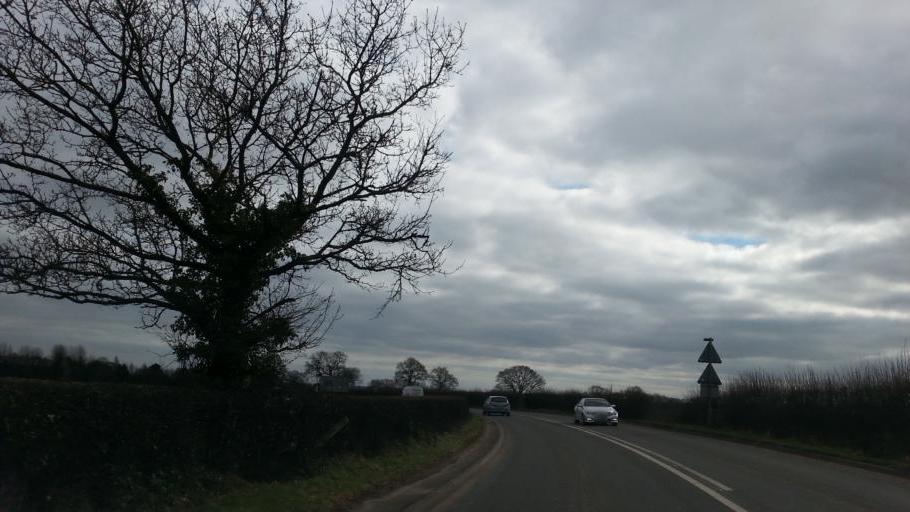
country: GB
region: England
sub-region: Staffordshire
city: Colwich
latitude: 52.8370
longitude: -2.0320
